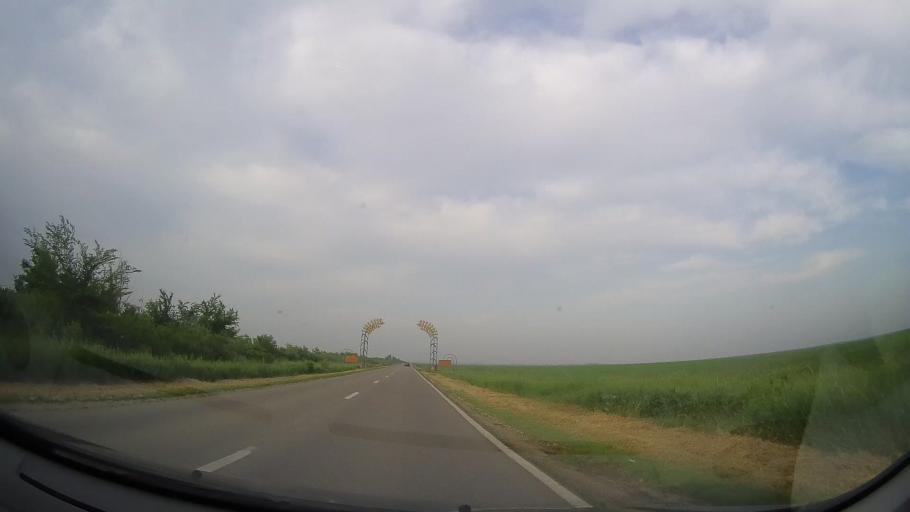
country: RO
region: Timis
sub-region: Comuna Parta
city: Parta
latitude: 45.6309
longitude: 21.0996
